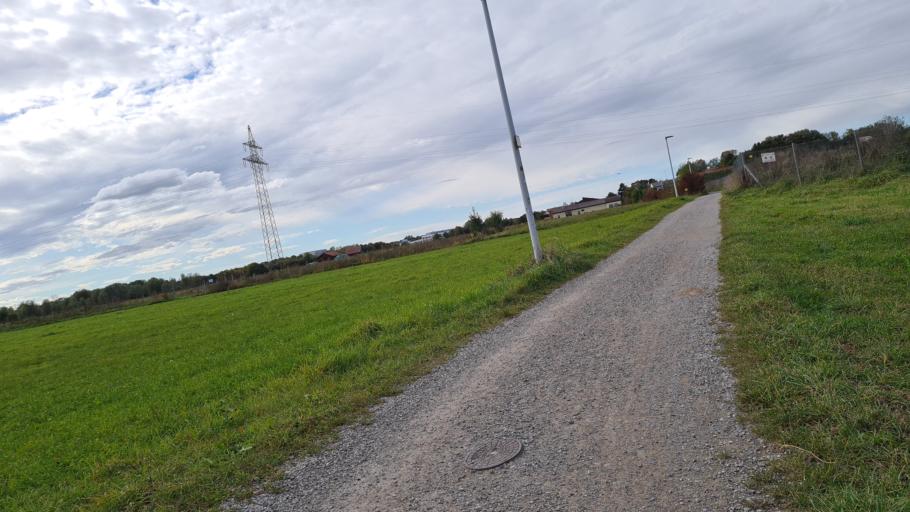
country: DE
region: Bavaria
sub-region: Upper Bavaria
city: Grafelfing
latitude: 48.1092
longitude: 11.4462
